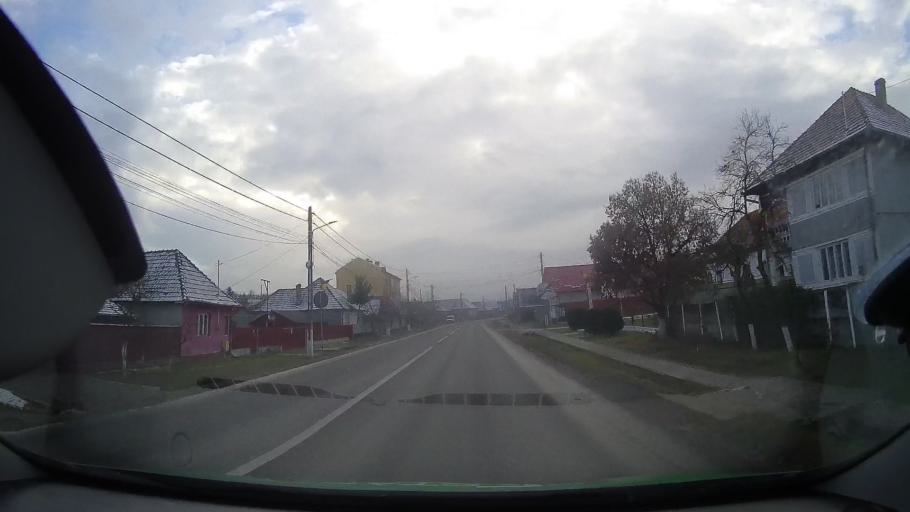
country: RO
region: Mures
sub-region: Comuna Cucerdea
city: Cucerdea
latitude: 46.4049
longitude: 24.2644
